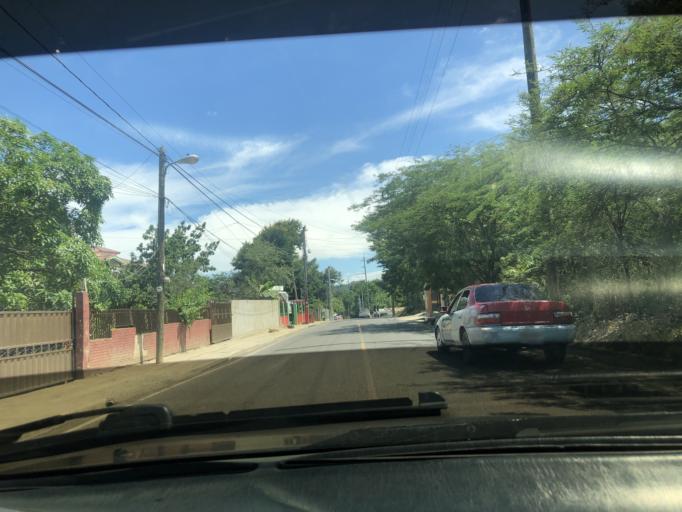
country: DO
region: Santiago
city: Santiago de los Caballeros
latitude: 19.4059
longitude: -70.6704
